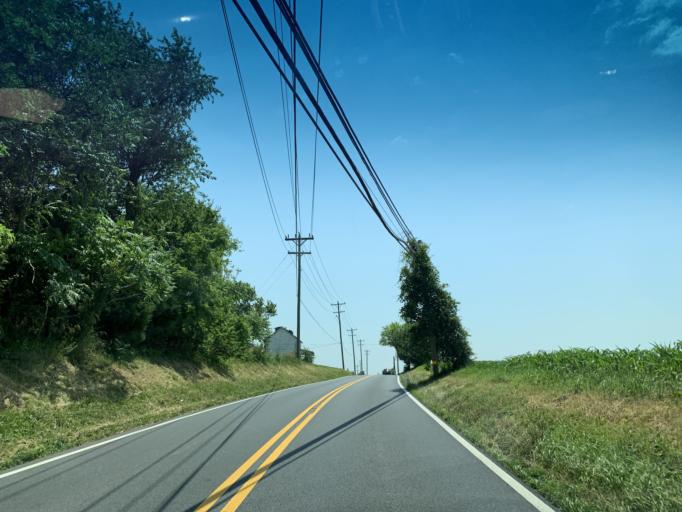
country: US
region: Maryland
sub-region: Frederick County
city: Green Valley
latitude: 39.3522
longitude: -77.2701
